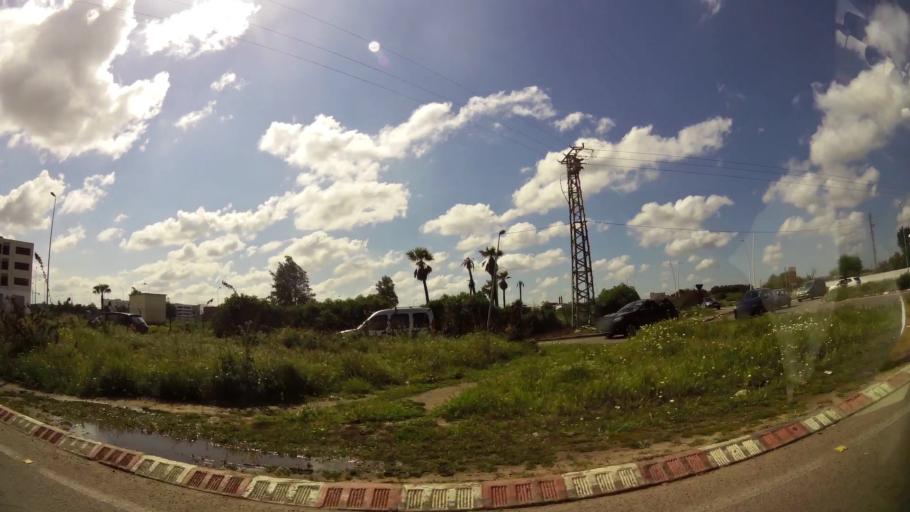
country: MA
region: Grand Casablanca
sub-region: Mediouna
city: Mediouna
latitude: 33.4091
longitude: -7.5333
